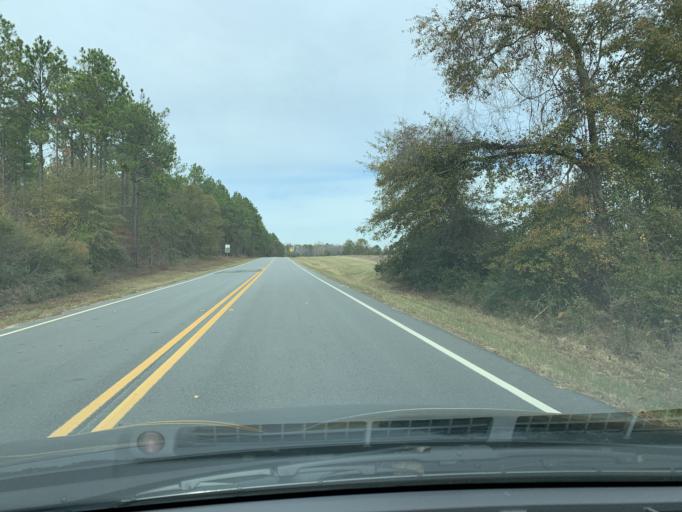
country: US
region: Georgia
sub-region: Wilcox County
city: Rochelle
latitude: 31.8337
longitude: -83.4290
